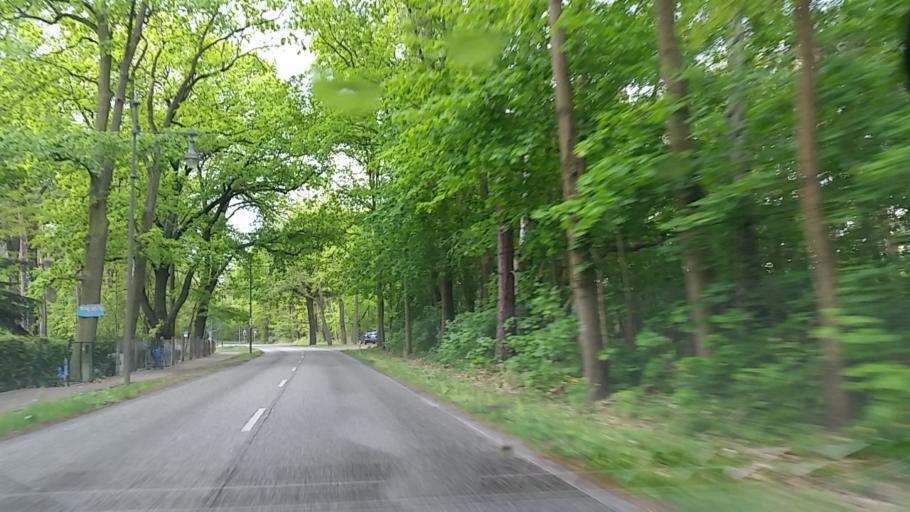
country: DE
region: Brandenburg
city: Diensdorf-Radlow
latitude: 52.2720
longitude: 14.0396
